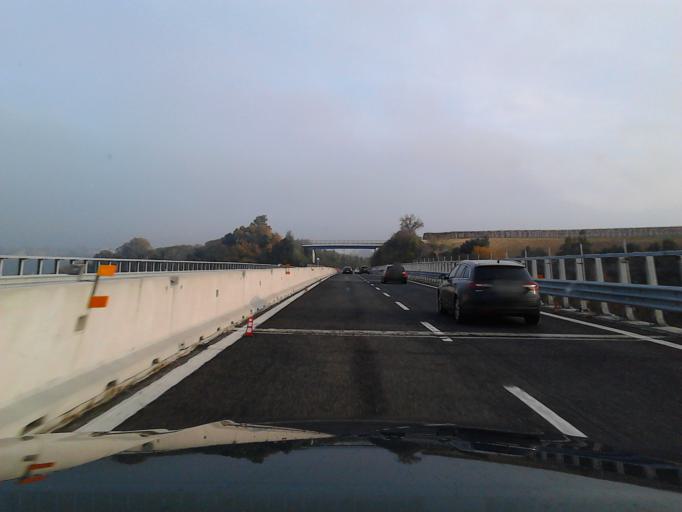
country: IT
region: Abruzzo
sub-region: Provincia di Chieti
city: San Vito Chietino
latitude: 42.2999
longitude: 14.4267
